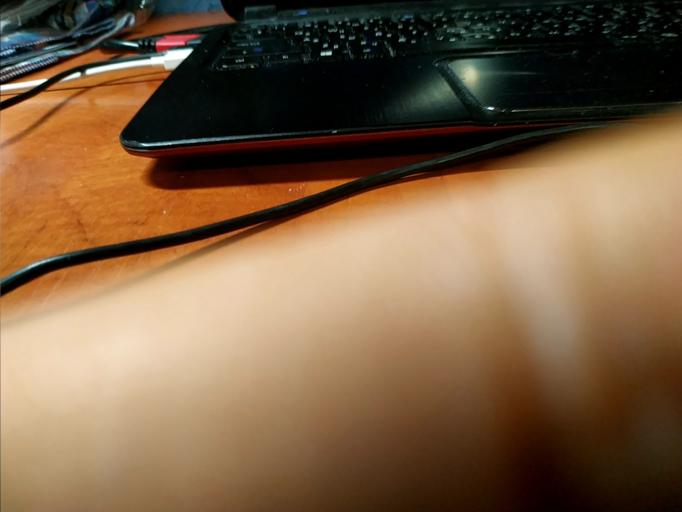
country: RU
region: Tverskaya
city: Spirovo
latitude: 57.3625
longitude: 34.9549
